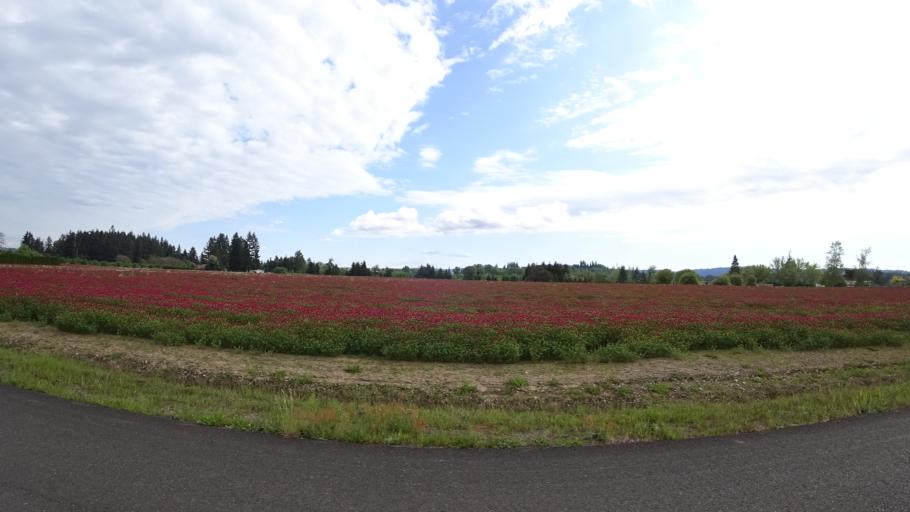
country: US
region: Oregon
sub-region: Washington County
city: Hillsboro
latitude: 45.4744
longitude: -122.9522
